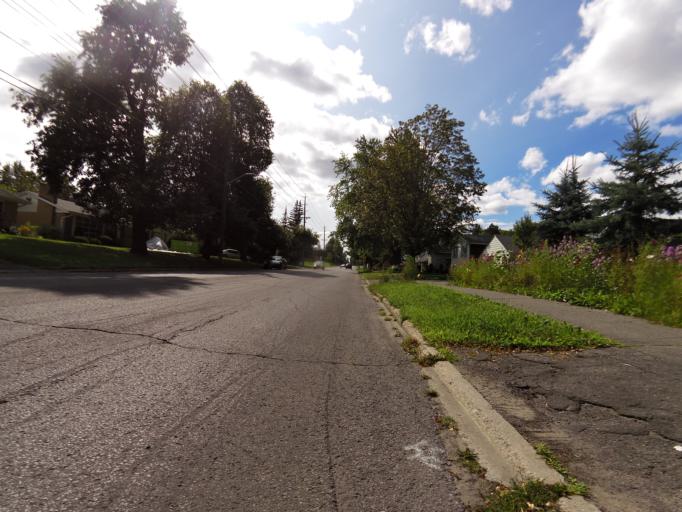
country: CA
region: Ontario
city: Ottawa
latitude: 45.3878
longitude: -75.6464
